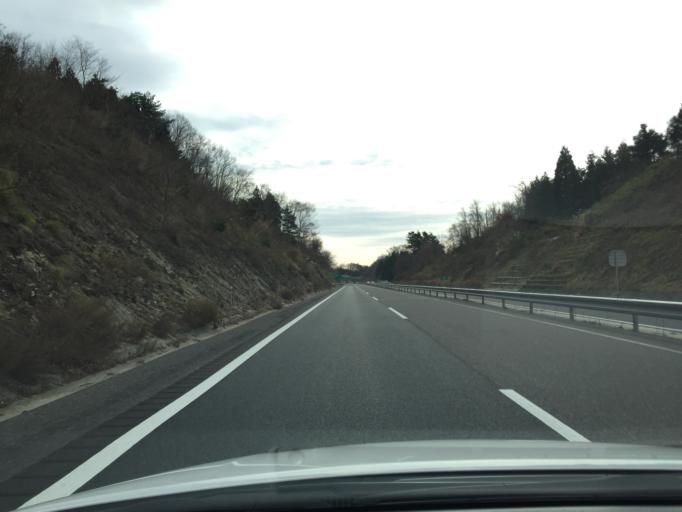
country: JP
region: Fukushima
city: Funehikimachi-funehiki
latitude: 37.4067
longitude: 140.5680
